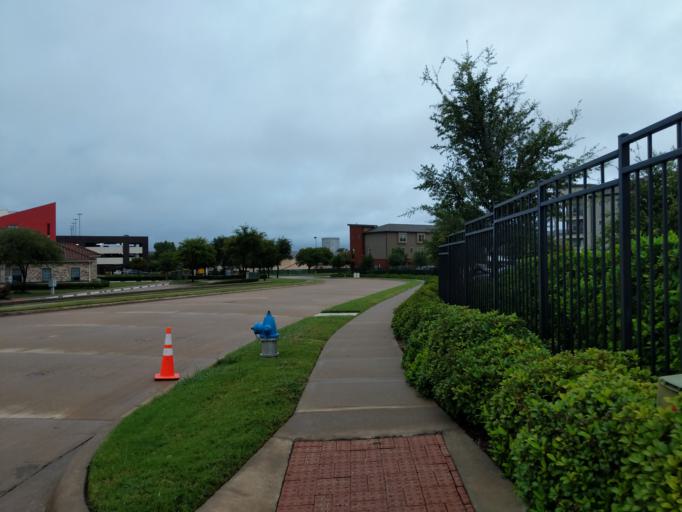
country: US
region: Texas
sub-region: Dallas County
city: Richardson
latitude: 33.0044
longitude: -96.7635
